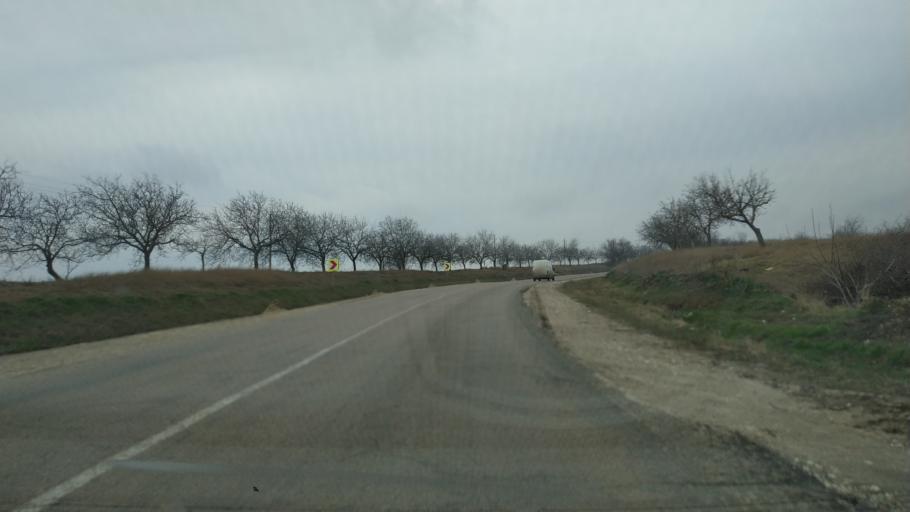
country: MD
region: Cahul
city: Cahul
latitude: 45.9542
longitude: 28.3977
